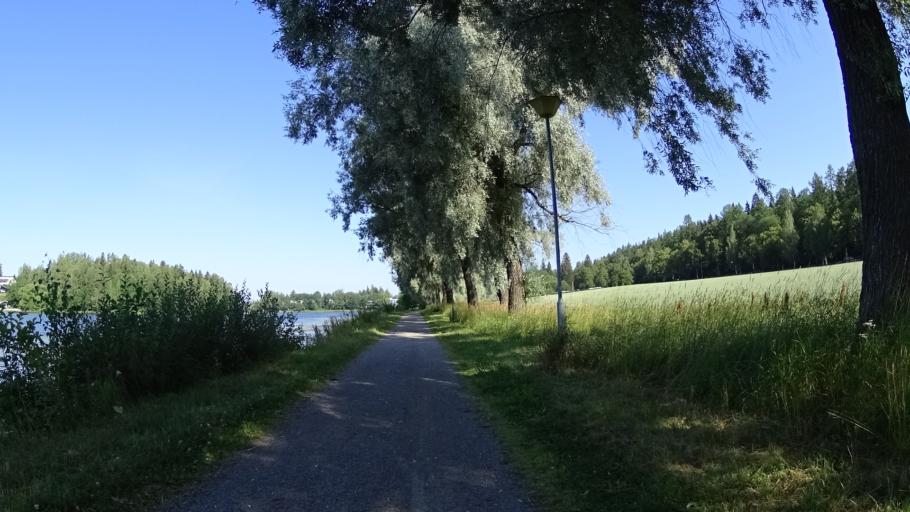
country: FI
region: Haeme
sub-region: Haemeenlinna
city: Haemeenlinna
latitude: 61.0166
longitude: 24.4494
